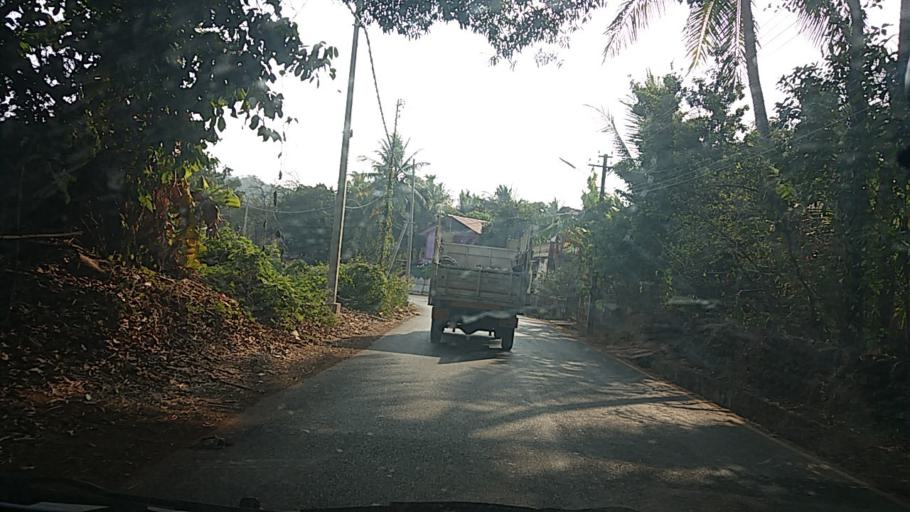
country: IN
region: Goa
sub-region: North Goa
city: Goa Velha
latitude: 15.4673
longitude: 73.9235
